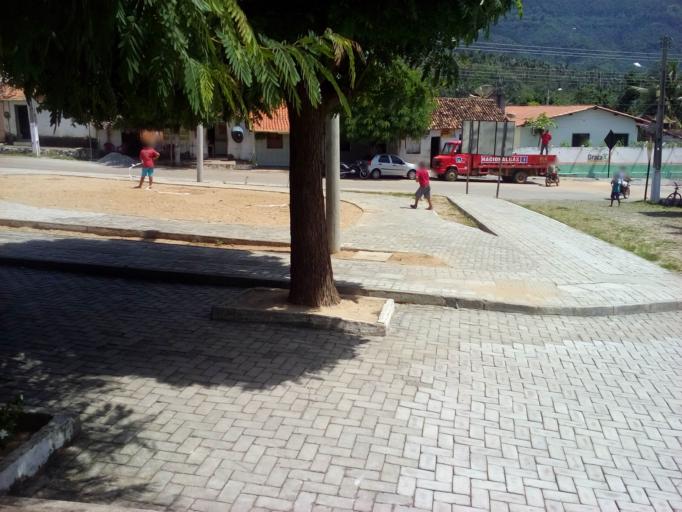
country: BR
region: Ceara
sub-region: Guaraciaba Do Norte
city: Guaraciaba do Norte
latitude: -4.0849
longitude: -40.8227
